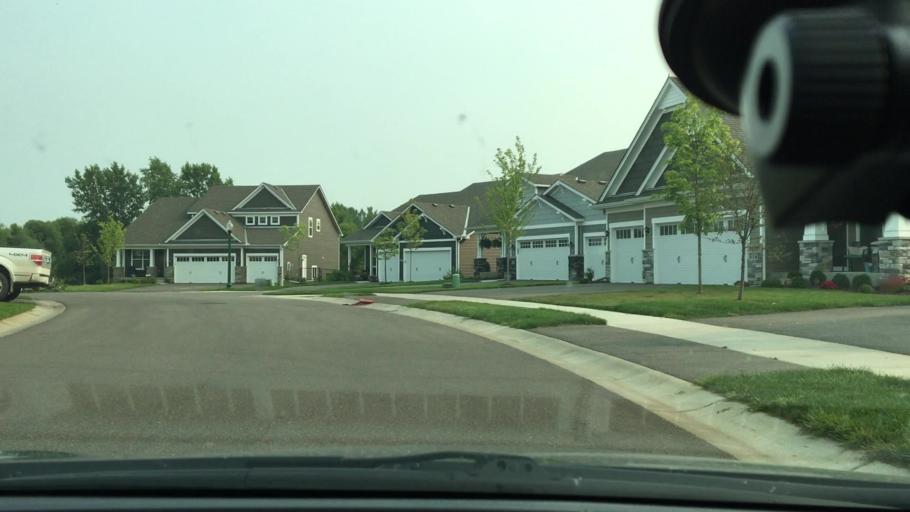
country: US
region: Minnesota
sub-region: Hennepin County
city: Champlin
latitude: 45.1974
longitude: -93.4367
